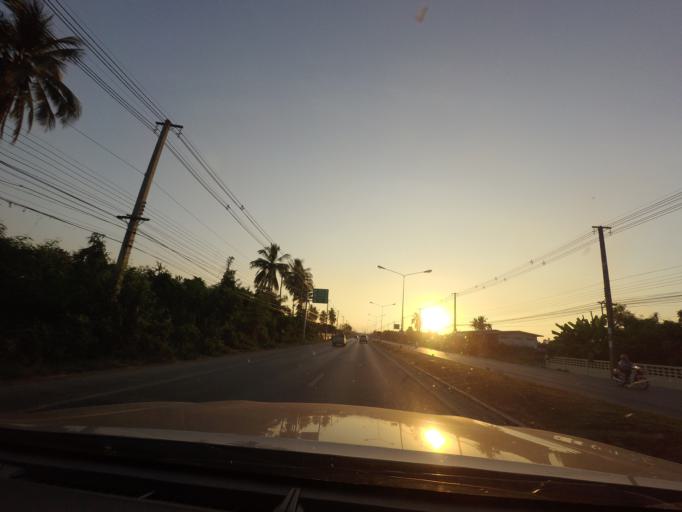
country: TH
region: Sukhothai
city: Sukhothai
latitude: 17.0530
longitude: 99.8285
